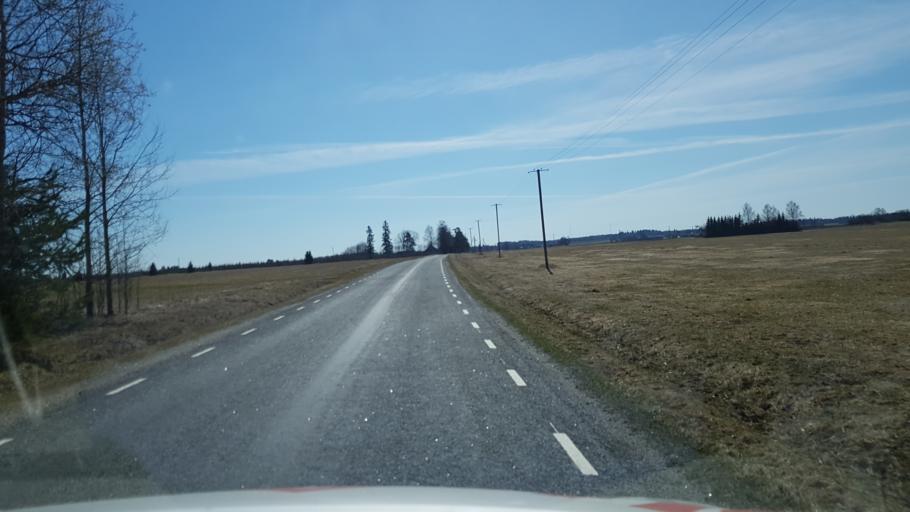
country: EE
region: Laeaene-Virumaa
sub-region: Vinni vald
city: Vinni
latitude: 59.1228
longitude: 26.5220
